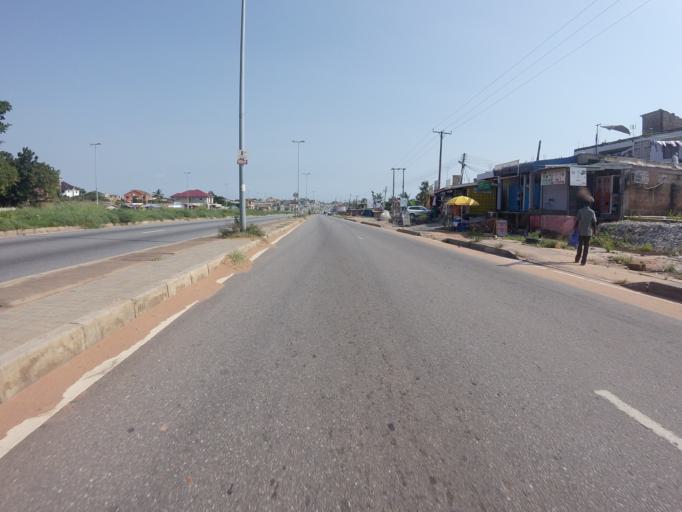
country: GH
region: Greater Accra
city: Gbawe
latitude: 5.6059
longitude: -0.2955
